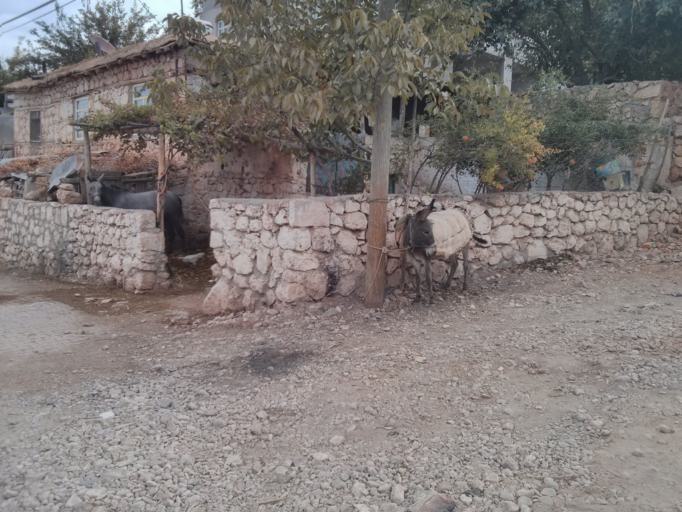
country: TR
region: Adiyaman
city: Damlacik
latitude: 37.9161
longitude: 38.6545
